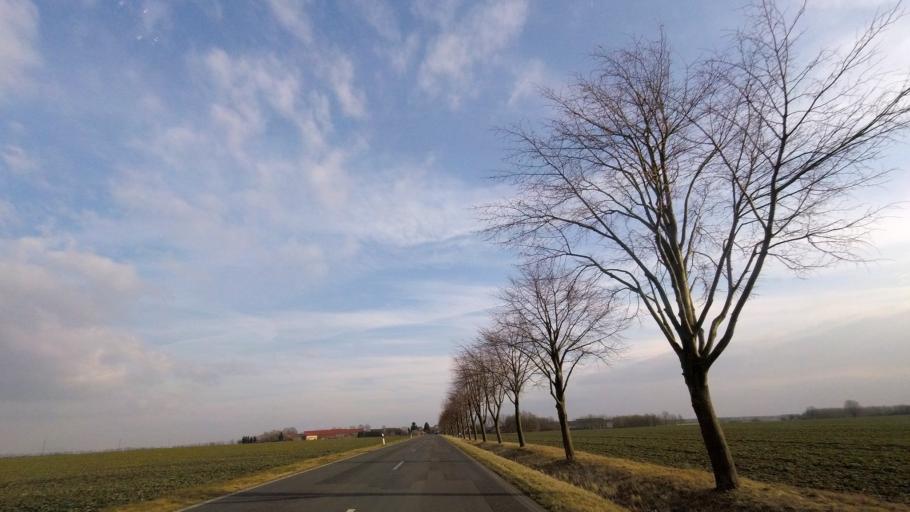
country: DE
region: Brandenburg
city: Belzig
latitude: 52.1057
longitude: 12.5472
